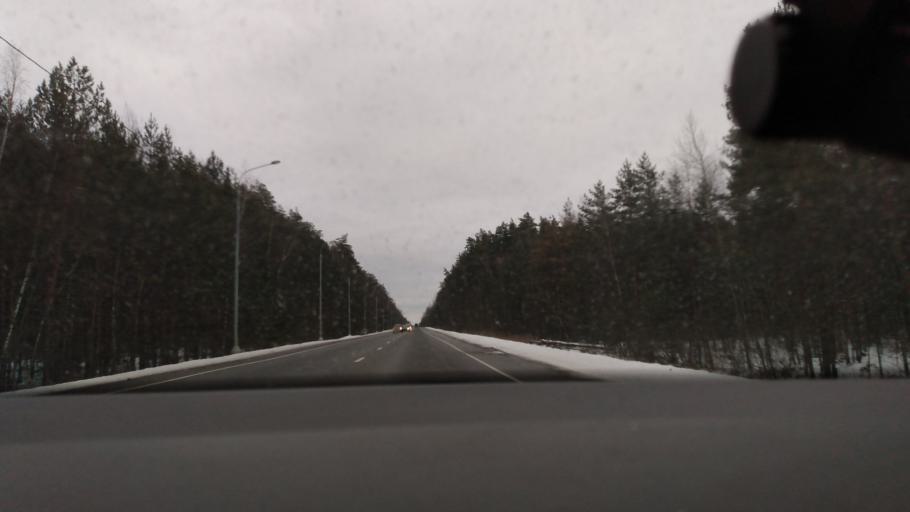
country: RU
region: Moskovskaya
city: Il'inskiy Pogost
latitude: 55.4678
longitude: 38.9679
